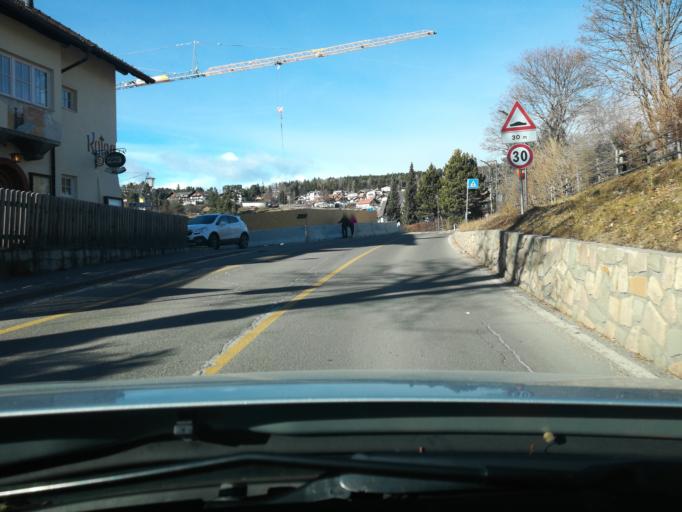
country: IT
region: Trentino-Alto Adige
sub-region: Bolzano
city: Collalbo
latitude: 46.5387
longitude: 11.4582
